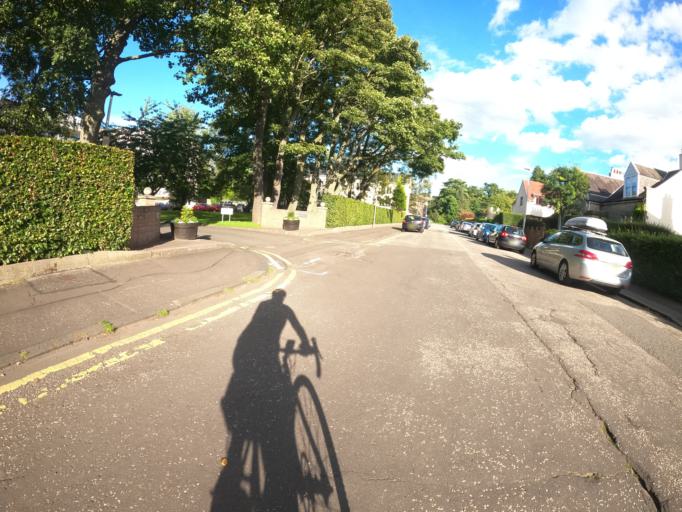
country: GB
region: Scotland
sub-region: Edinburgh
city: Currie
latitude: 55.9615
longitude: -3.3032
